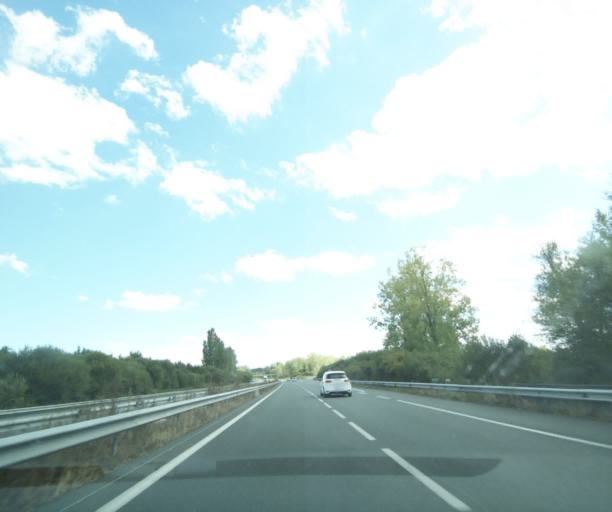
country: FR
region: Aquitaine
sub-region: Departement du Lot-et-Garonne
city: Fourques-sur-Garonne
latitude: 44.4330
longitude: 0.1294
